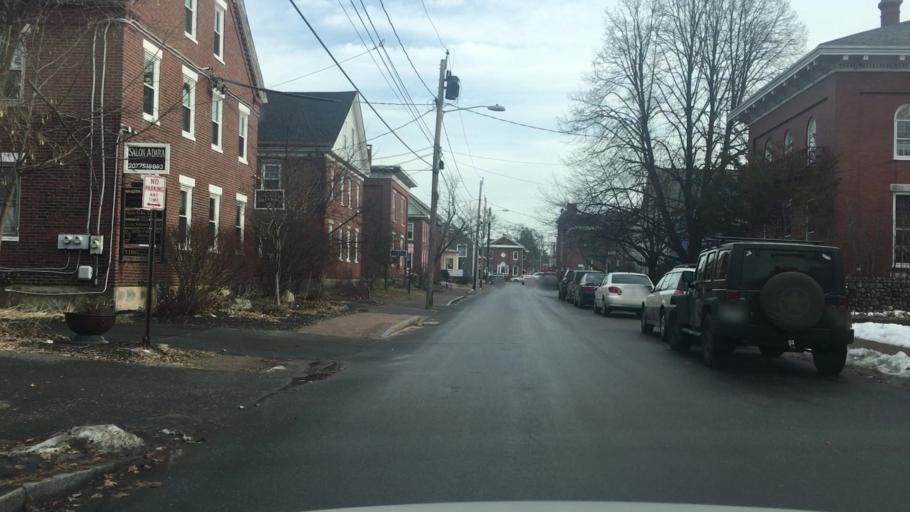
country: US
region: Maine
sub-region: Cumberland County
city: Brunswick
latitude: 43.9165
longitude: -69.9679
